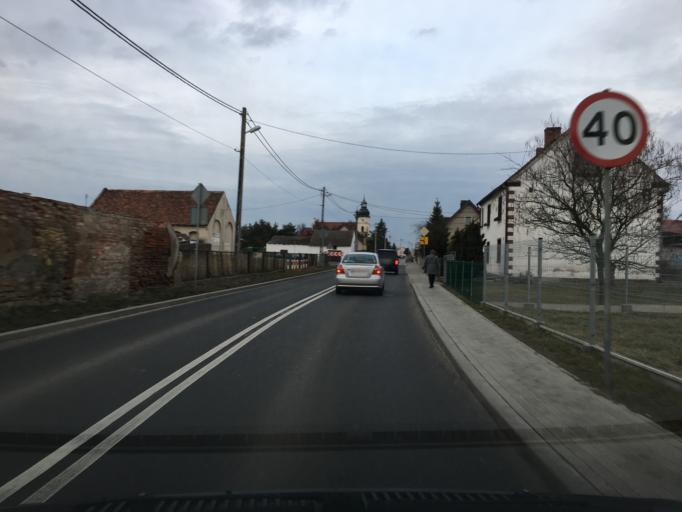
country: PL
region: Opole Voivodeship
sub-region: Powiat krapkowicki
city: Januszkowice
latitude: 50.3909
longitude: 18.1370
